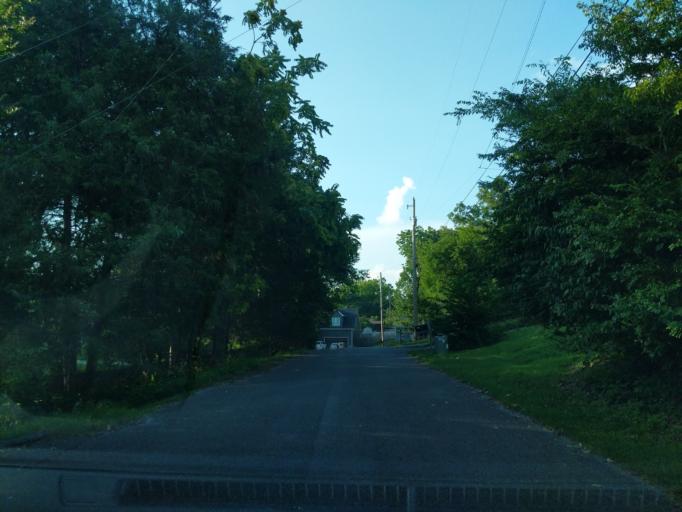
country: US
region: Tennessee
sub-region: Sumner County
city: Hendersonville
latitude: 36.2945
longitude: -86.6437
